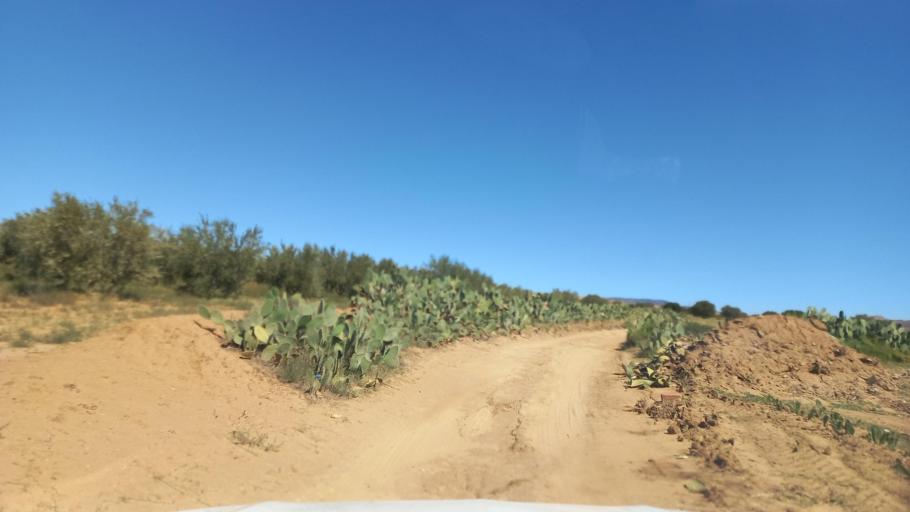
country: TN
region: Al Qasrayn
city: Sbiba
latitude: 35.3474
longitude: 9.0985
